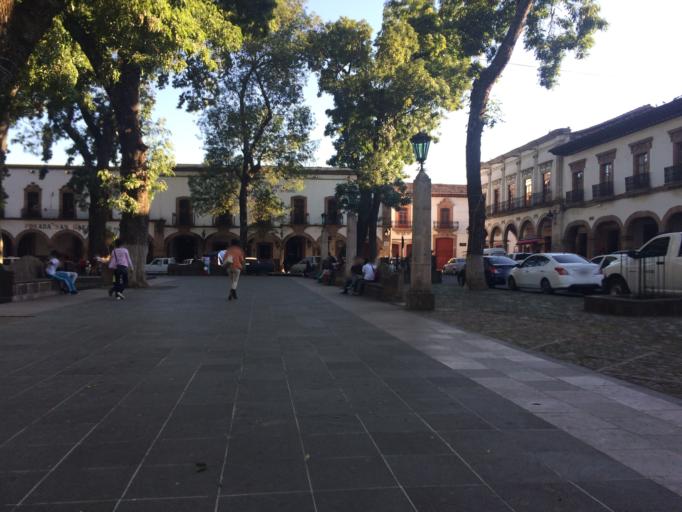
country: MX
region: Michoacan
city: Patzcuaro
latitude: 19.5137
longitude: -101.6097
